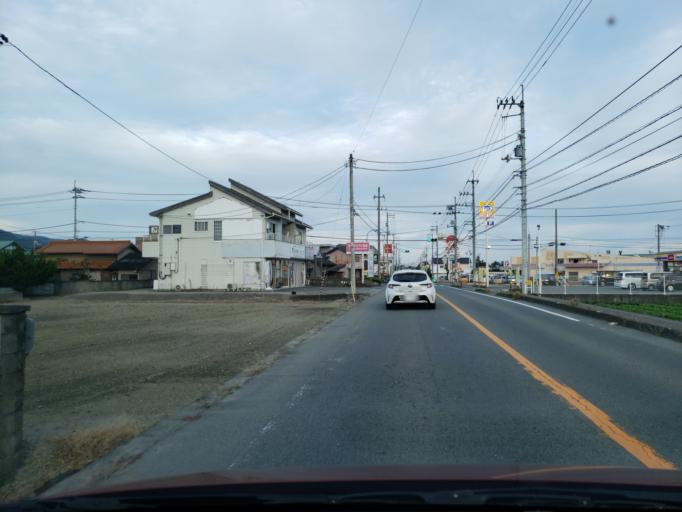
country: JP
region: Tokushima
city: Kamojimacho-jogejima
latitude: 34.0844
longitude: 134.2826
